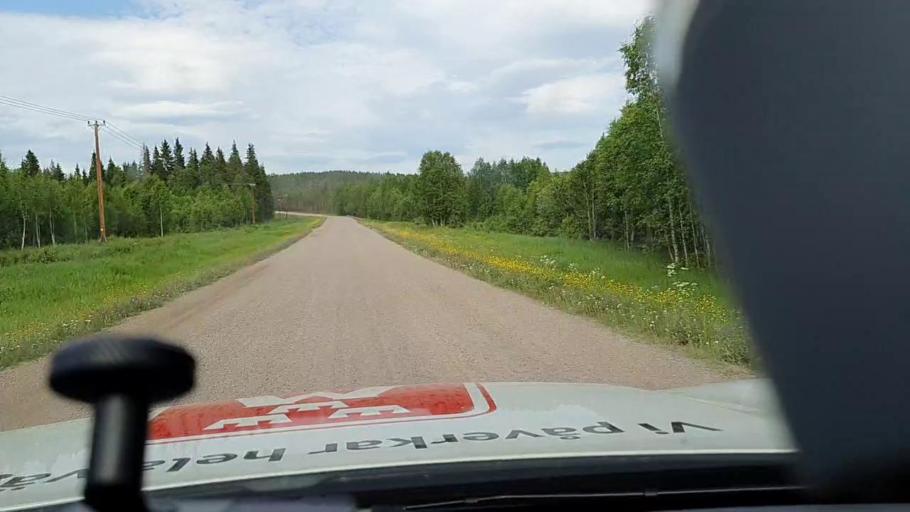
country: SE
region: Norrbotten
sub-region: Alvsbyns Kommun
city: AElvsbyn
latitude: 66.1198
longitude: 20.9846
